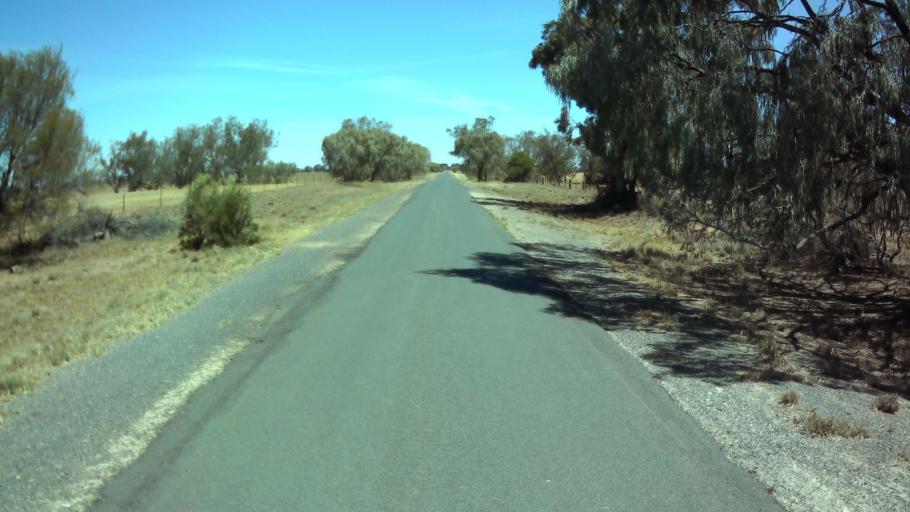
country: AU
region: New South Wales
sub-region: Weddin
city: Grenfell
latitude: -33.8478
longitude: 147.6961
